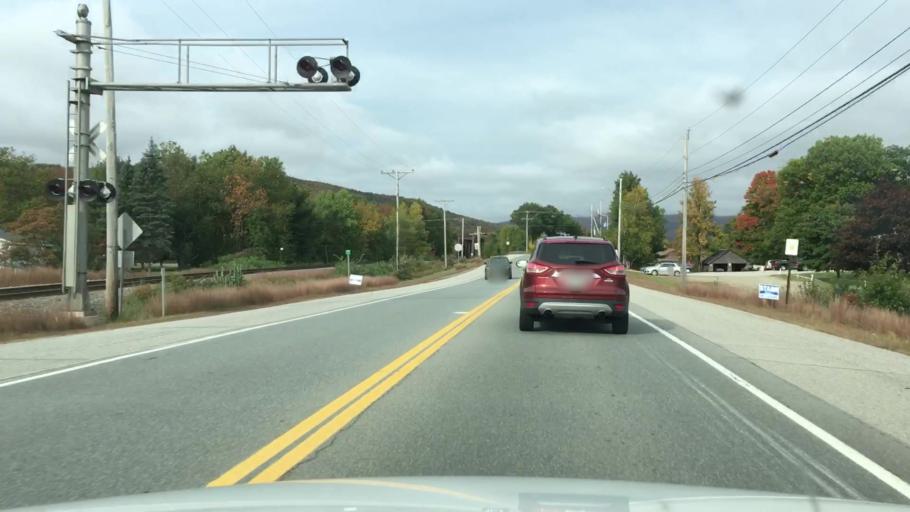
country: US
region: New Hampshire
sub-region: Coos County
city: Gorham
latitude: 44.3859
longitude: -71.1628
